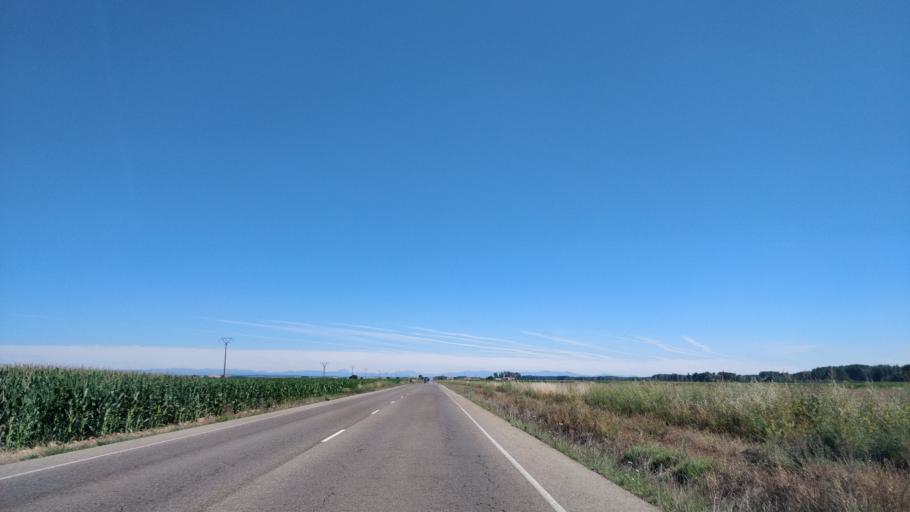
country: ES
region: Castille and Leon
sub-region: Provincia de Leon
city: Soto de la Vega
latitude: 42.3583
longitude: -5.8899
